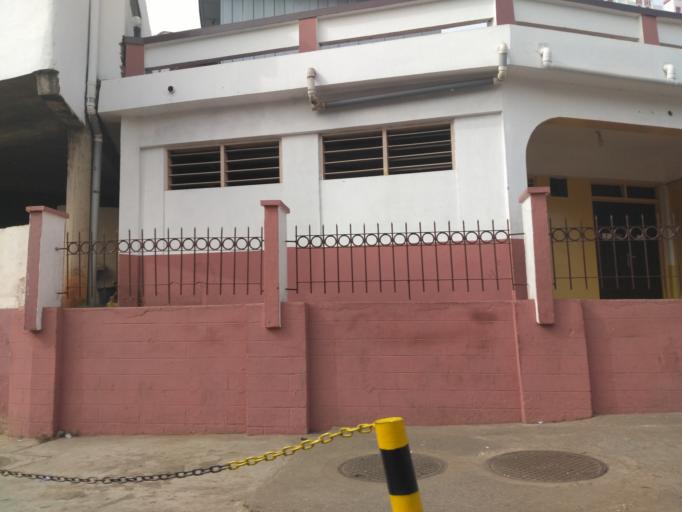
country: GH
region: Ashanti
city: Kumasi
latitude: 6.6939
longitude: -1.6232
